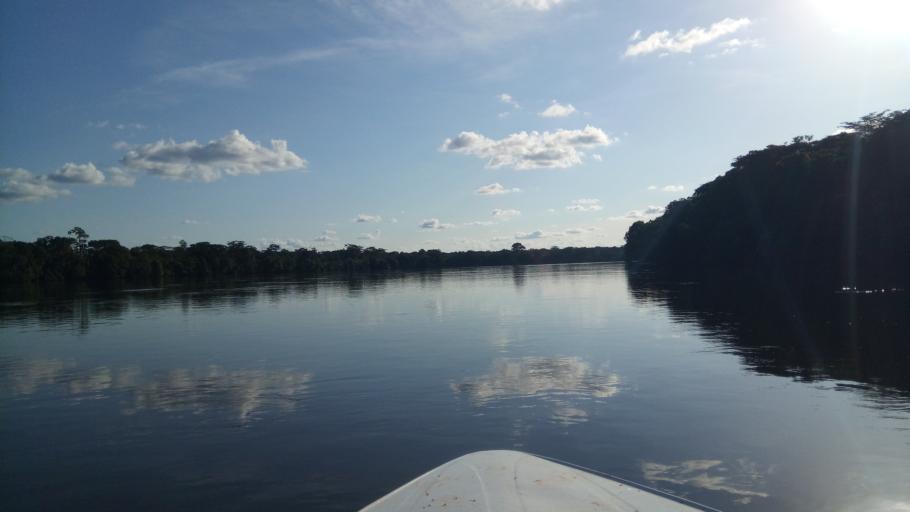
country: CD
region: Eastern Province
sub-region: Sous-Region de la Tshopo
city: Yangambi
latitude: 0.2344
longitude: 24.1052
